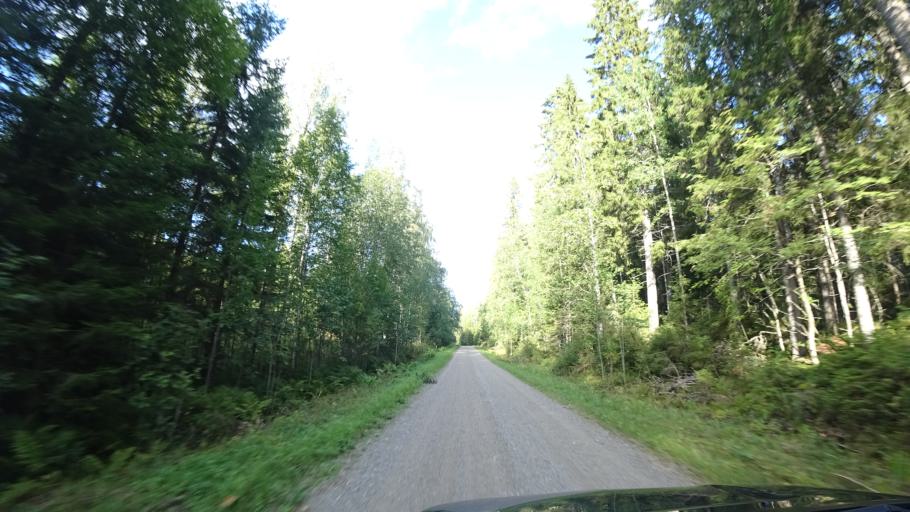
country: FI
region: Paijanne Tavastia
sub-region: Lahti
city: Auttoinen
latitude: 61.2201
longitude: 25.1799
